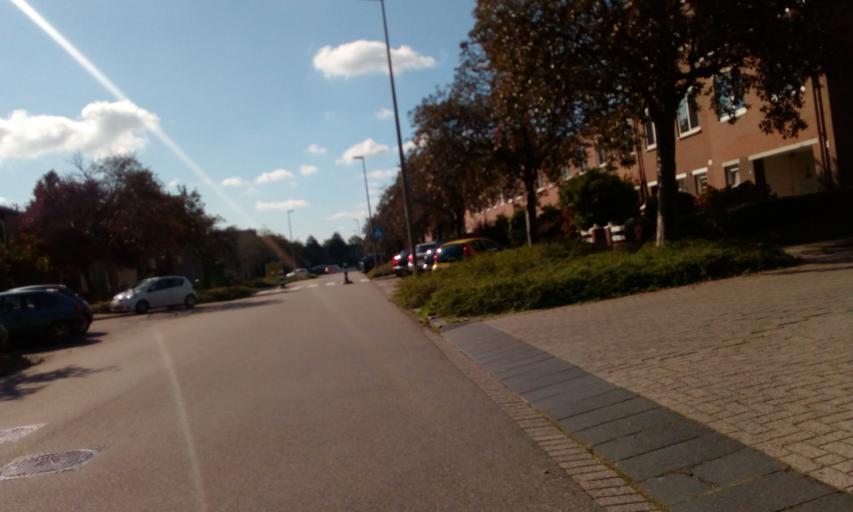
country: NL
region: South Holland
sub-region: Gemeente Zoetermeer
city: Zoetermeer
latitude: 52.0781
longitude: 4.5135
